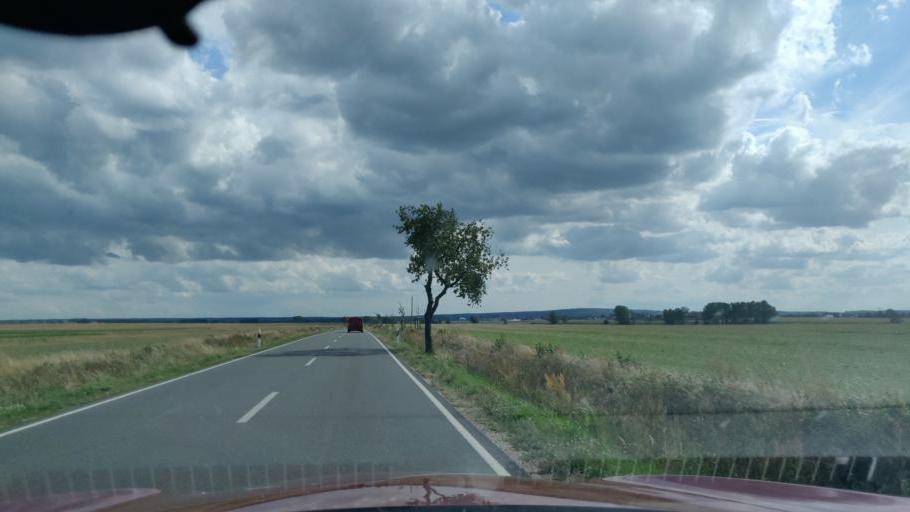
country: DE
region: Saxony
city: Schildau
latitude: 51.5087
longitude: 12.9101
